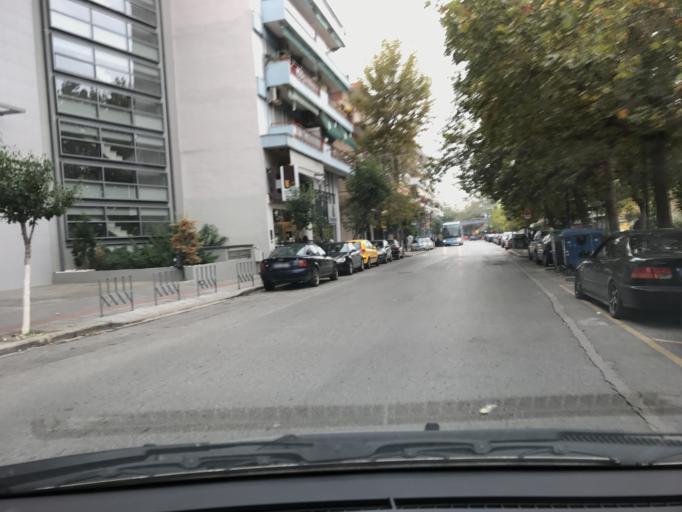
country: GR
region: Central Macedonia
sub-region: Nomos Thessalonikis
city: Ampelokipoi
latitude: 40.6543
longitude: 22.9233
